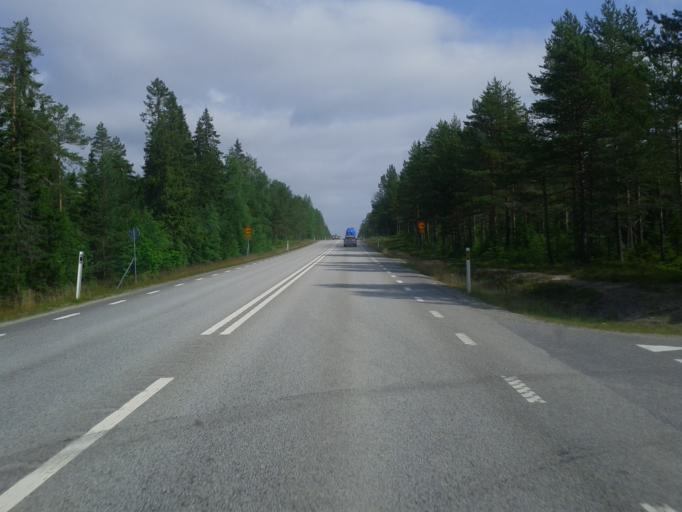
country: SE
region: Vaesterbotten
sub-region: Robertsfors Kommun
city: Robertsfors
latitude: 64.1925
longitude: 21.0021
